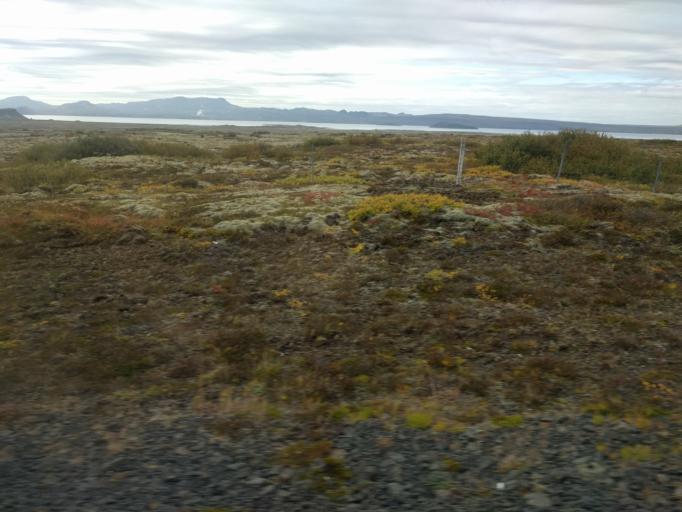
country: IS
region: South
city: Hveragerdi
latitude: 64.2018
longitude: -21.0351
